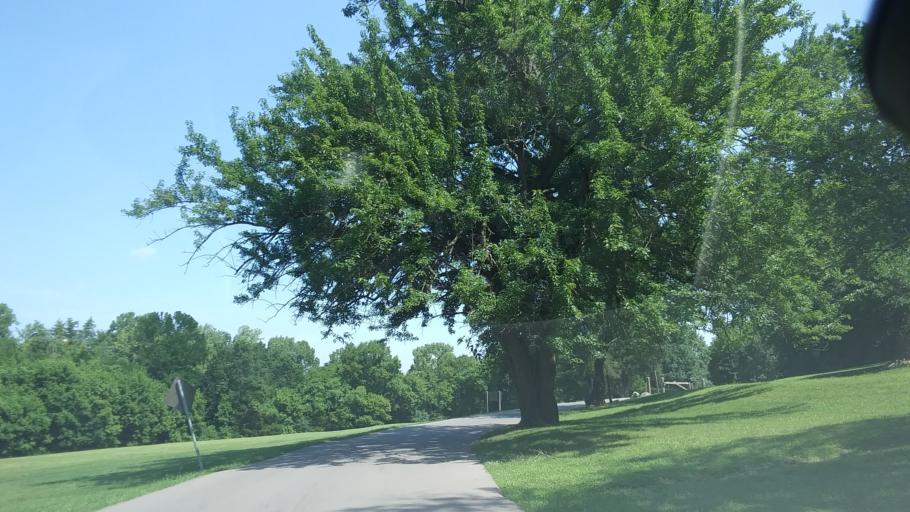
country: US
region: Tennessee
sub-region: Davidson County
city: Belle Meade
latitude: 36.0759
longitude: -86.8861
